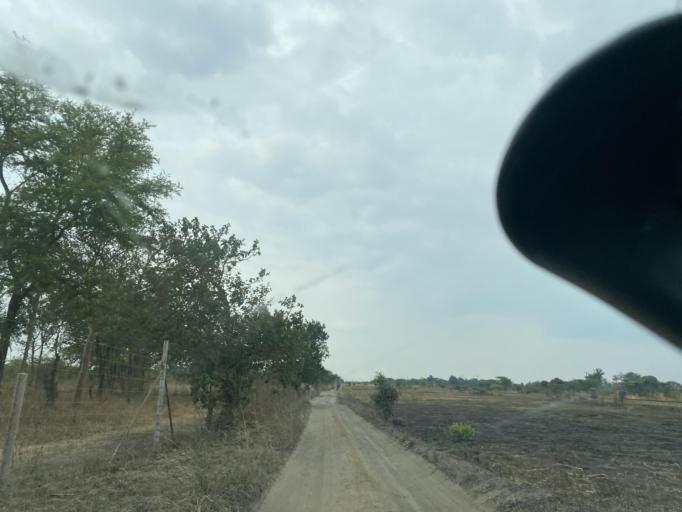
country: ZM
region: Lusaka
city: Lusaka
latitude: -15.2492
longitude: 28.3318
